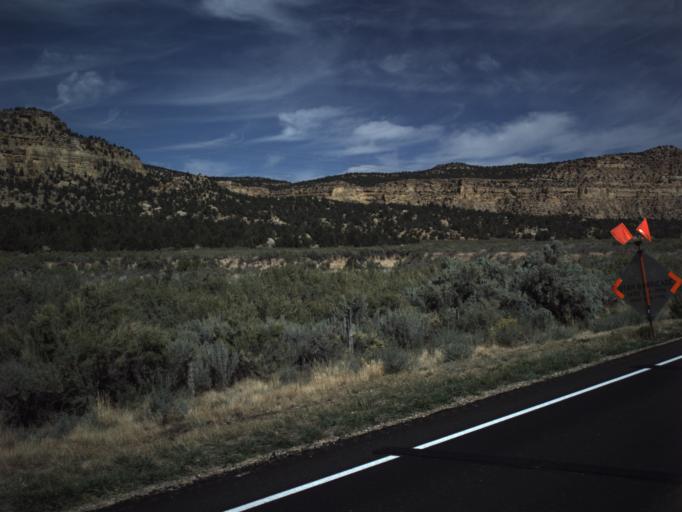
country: US
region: Utah
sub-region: Wayne County
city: Loa
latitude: 37.7489
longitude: -111.7040
